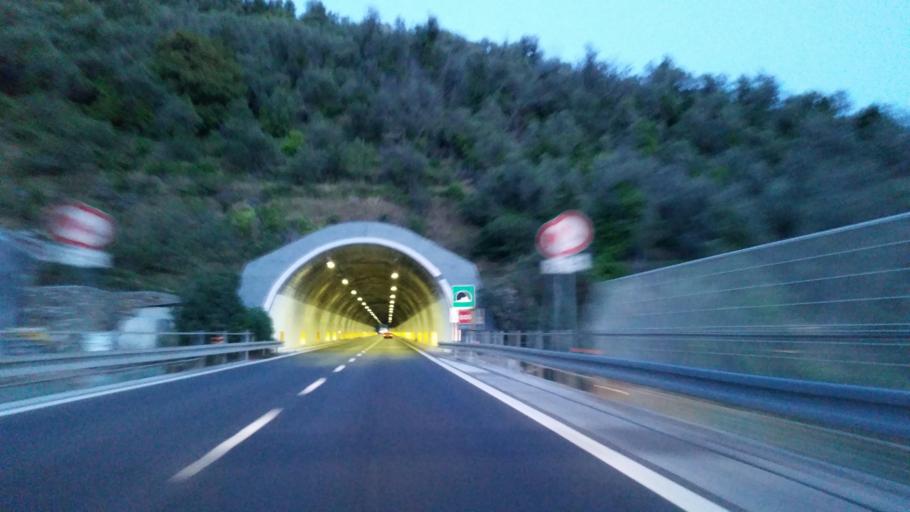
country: IT
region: Liguria
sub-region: Provincia di Imperia
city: Terzorio
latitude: 43.8547
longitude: 7.8984
